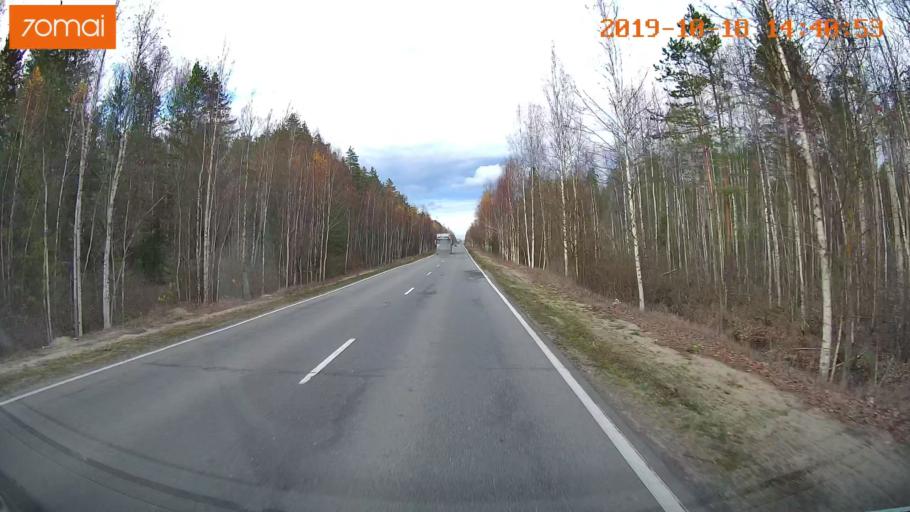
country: RU
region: Vladimir
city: Velikodvorskiy
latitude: 55.2835
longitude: 40.6698
